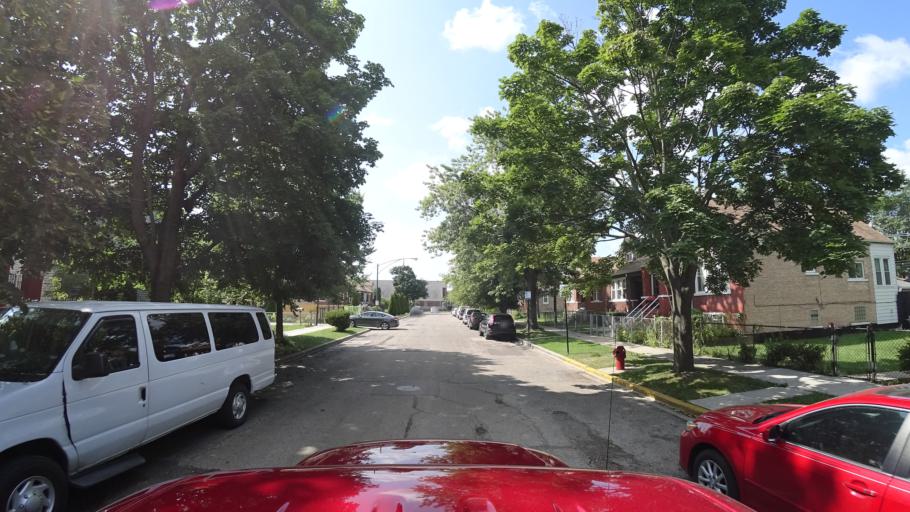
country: US
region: Illinois
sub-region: Cook County
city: Cicero
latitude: 41.8345
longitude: -87.7255
